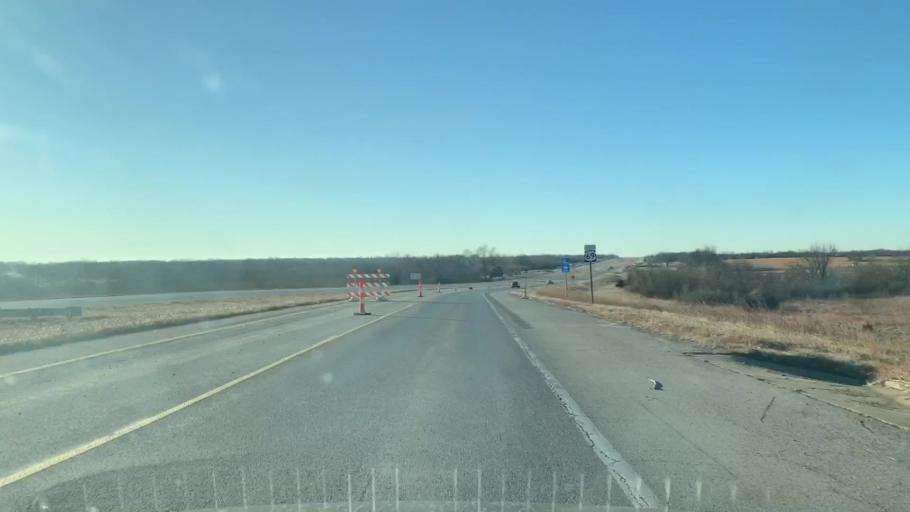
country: US
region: Kansas
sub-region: Bourbon County
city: Fort Scott
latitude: 37.7668
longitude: -94.7053
